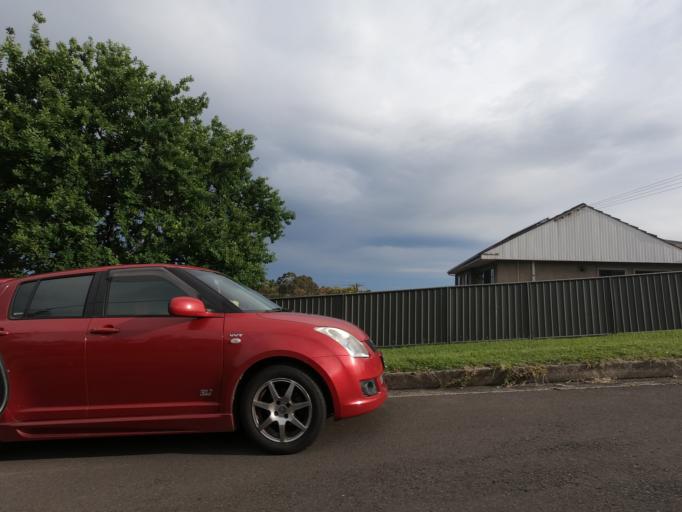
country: AU
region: New South Wales
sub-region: Wollongong
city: Lake Heights
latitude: -34.4890
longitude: 150.8729
